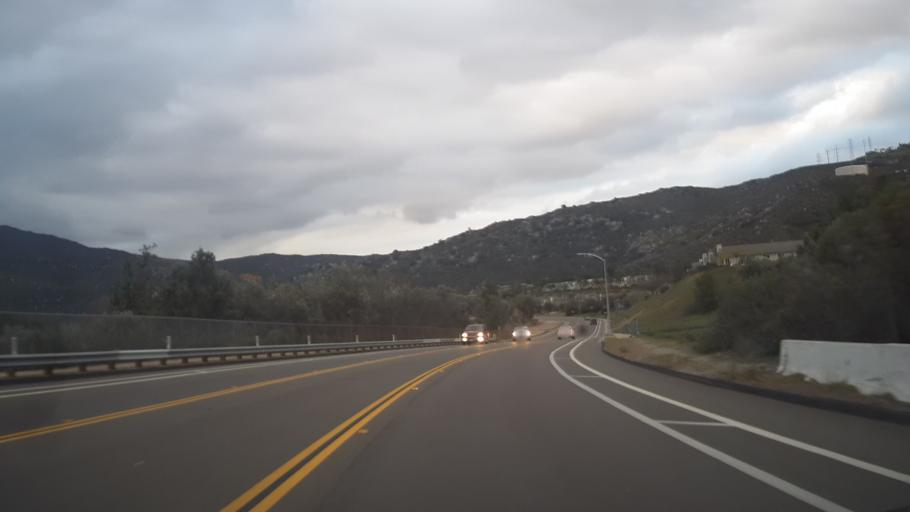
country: US
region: California
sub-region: San Diego County
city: Granite Hills
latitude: 32.7804
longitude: -116.8887
